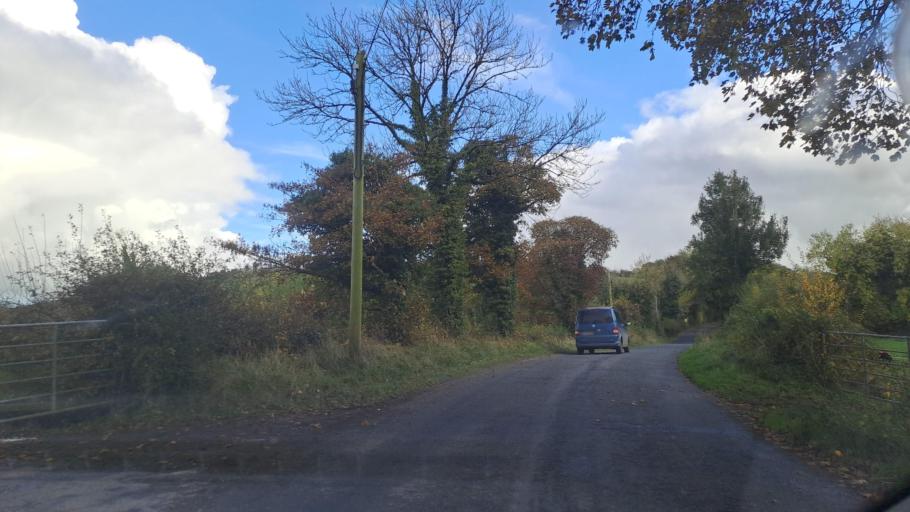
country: IE
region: Ulster
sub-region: An Cabhan
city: Bailieborough
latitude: 53.9968
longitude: -6.9549
